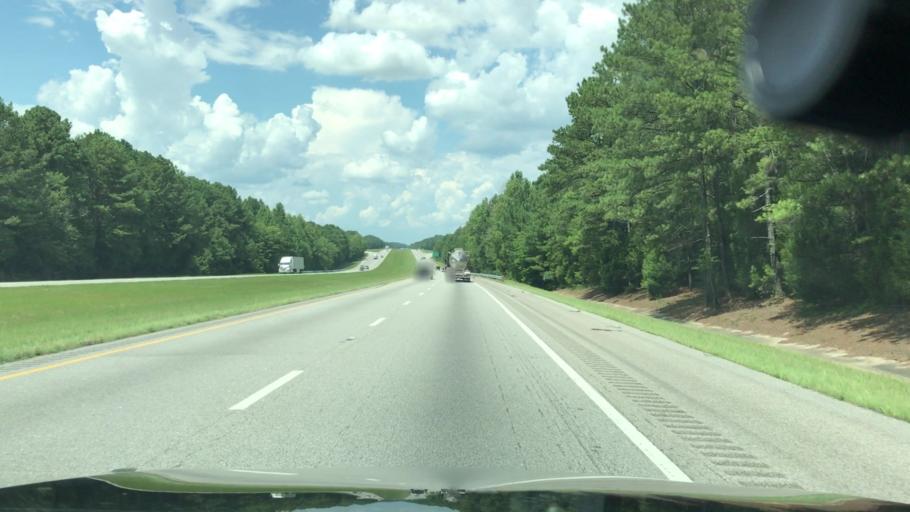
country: US
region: South Carolina
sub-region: Chester County
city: Eureka Mill
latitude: 34.7016
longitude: -81.0296
